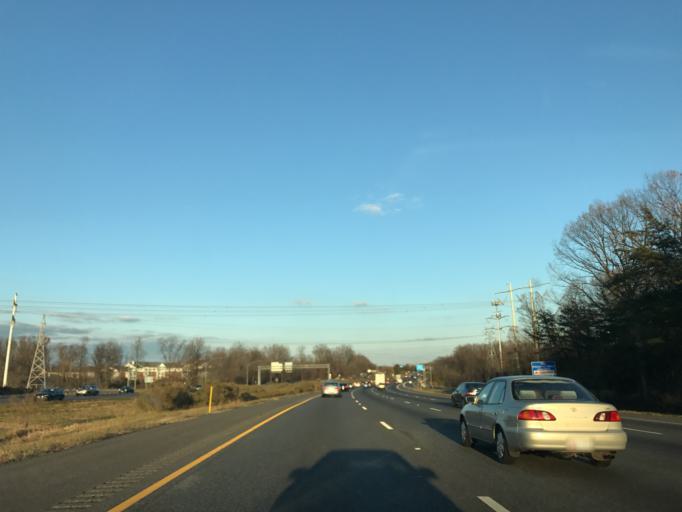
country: US
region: Maryland
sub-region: Howard County
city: North Laurel
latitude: 39.1318
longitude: -76.8593
